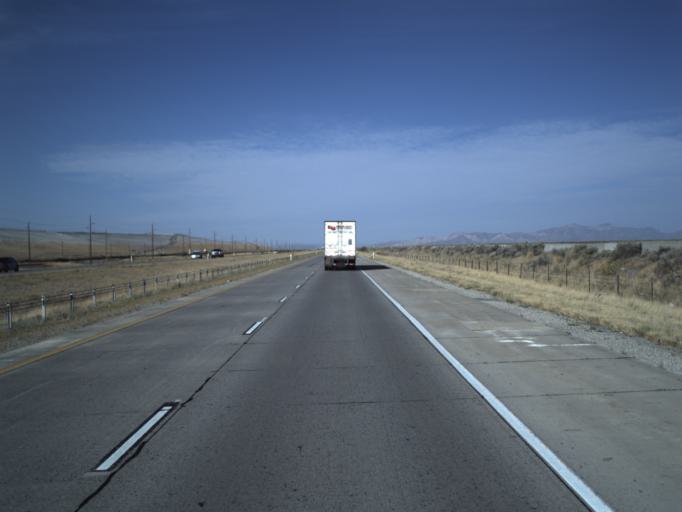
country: US
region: Utah
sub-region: Salt Lake County
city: Magna
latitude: 40.7710
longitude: -112.1038
